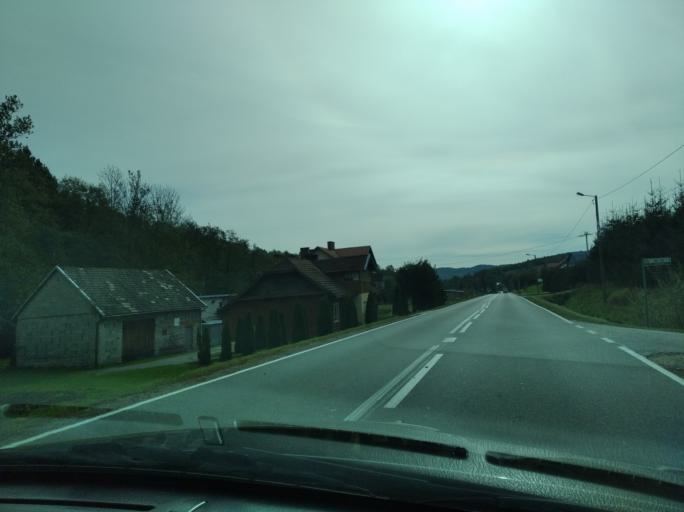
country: PL
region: Subcarpathian Voivodeship
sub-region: Powiat strzyzowski
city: Wisniowa
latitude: 49.8951
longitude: 21.6431
